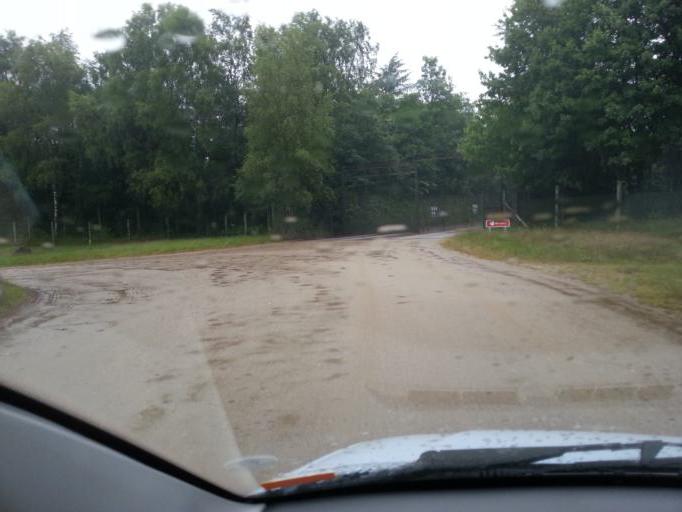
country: DK
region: South Denmark
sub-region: Vejle Kommune
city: Jelling
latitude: 55.8090
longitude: 9.3544
